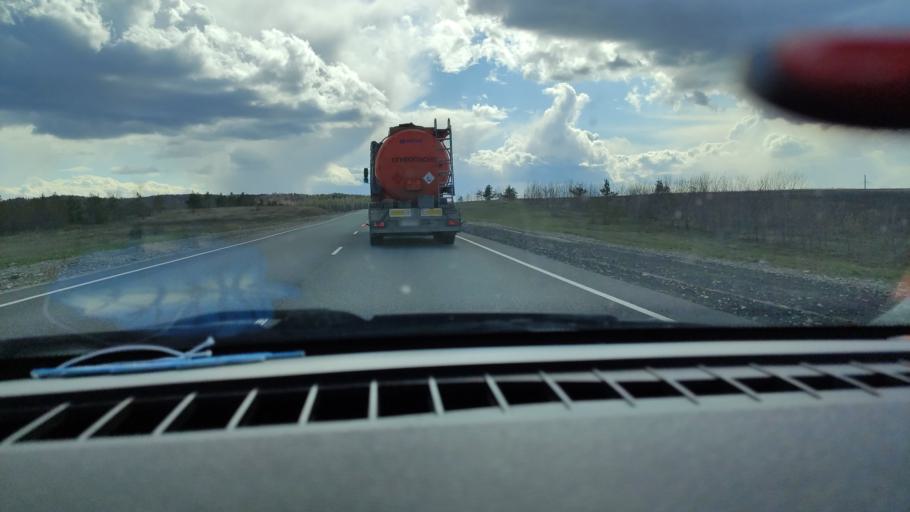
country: RU
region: Saratov
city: Khvalynsk
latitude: 52.5494
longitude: 48.0726
